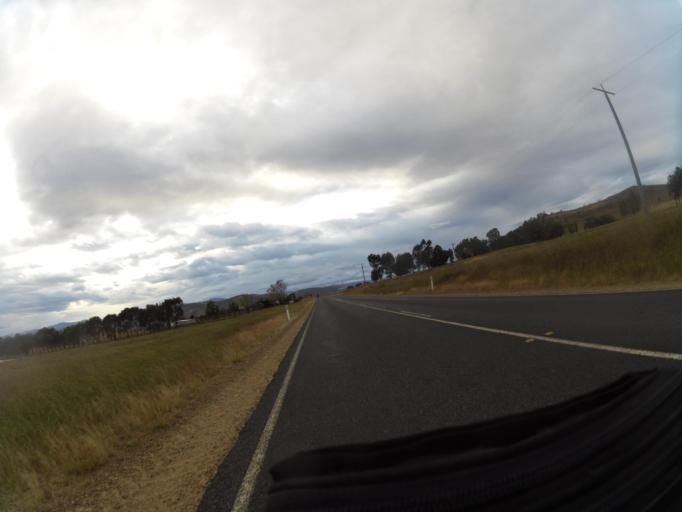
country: AU
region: New South Wales
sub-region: Greater Hume Shire
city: Holbrook
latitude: -36.0709
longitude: 147.9622
